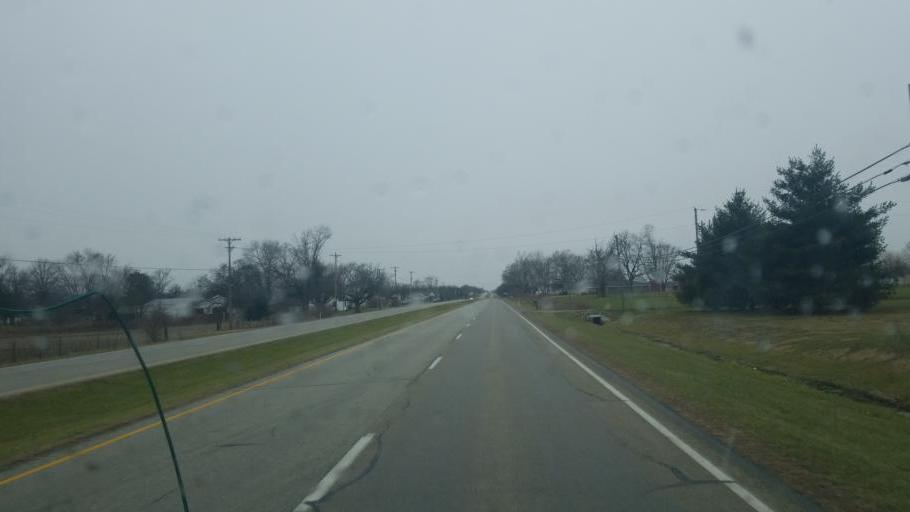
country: US
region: Indiana
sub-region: Hancock County
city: Greenfield
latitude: 39.7881
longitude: -85.7047
